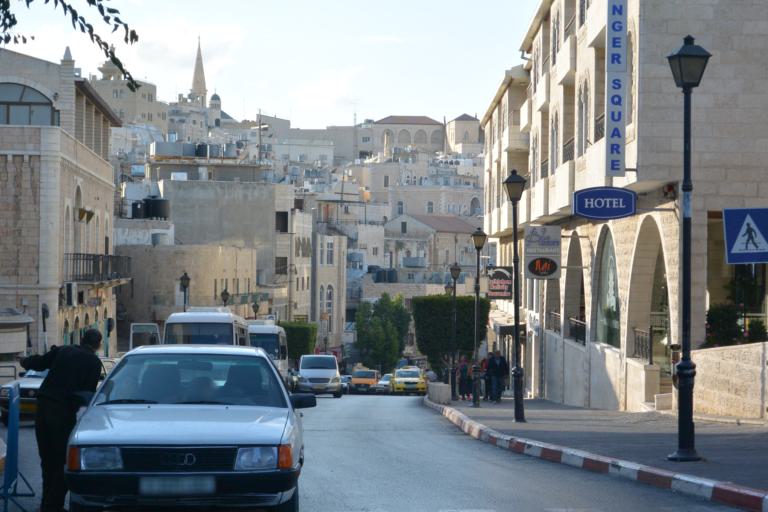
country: PS
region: West Bank
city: Bethlehem
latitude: 31.7049
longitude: 35.2064
